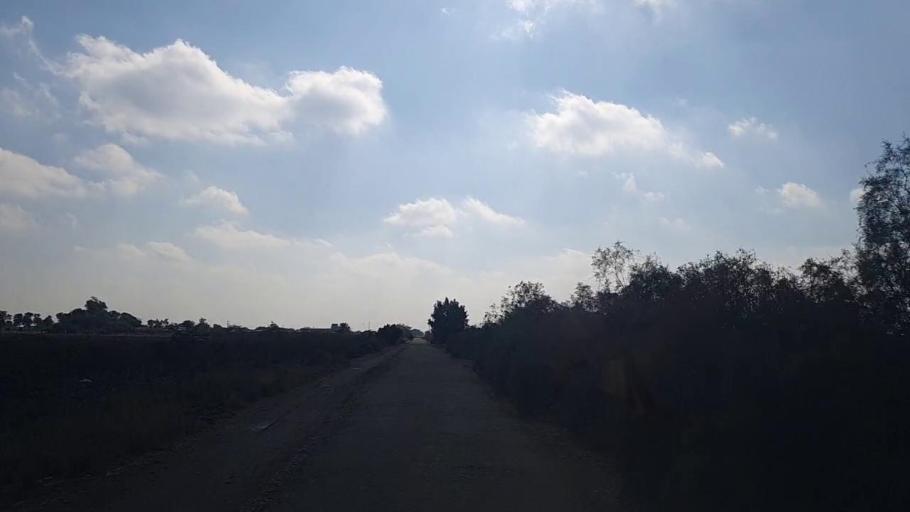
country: PK
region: Sindh
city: Sanghar
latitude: 26.0633
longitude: 69.0274
